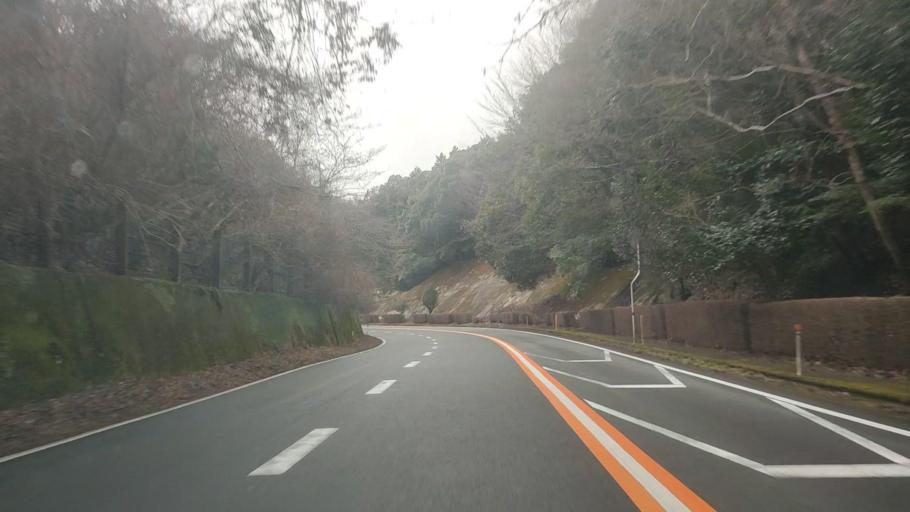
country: JP
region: Kumamoto
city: Hitoyoshi
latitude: 32.1187
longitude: 130.8119
